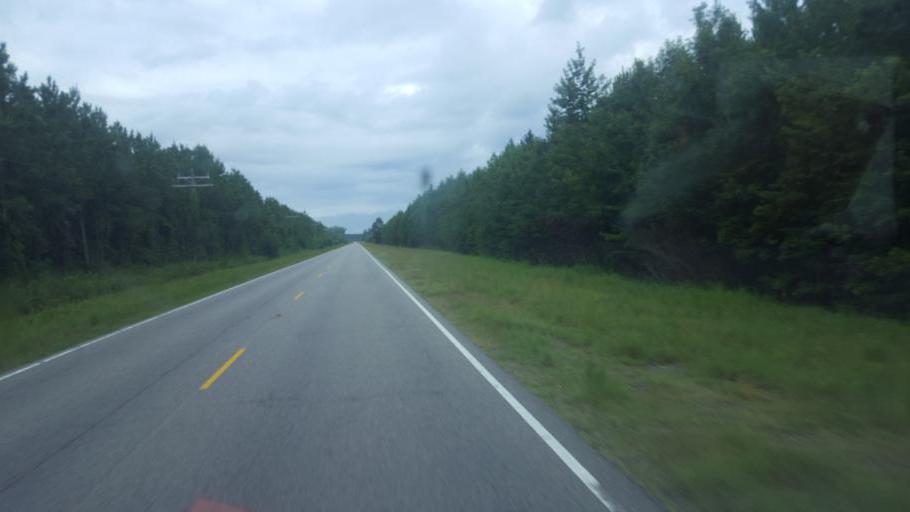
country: US
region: North Carolina
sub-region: Tyrrell County
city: Columbia
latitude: 35.9332
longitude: -76.1680
